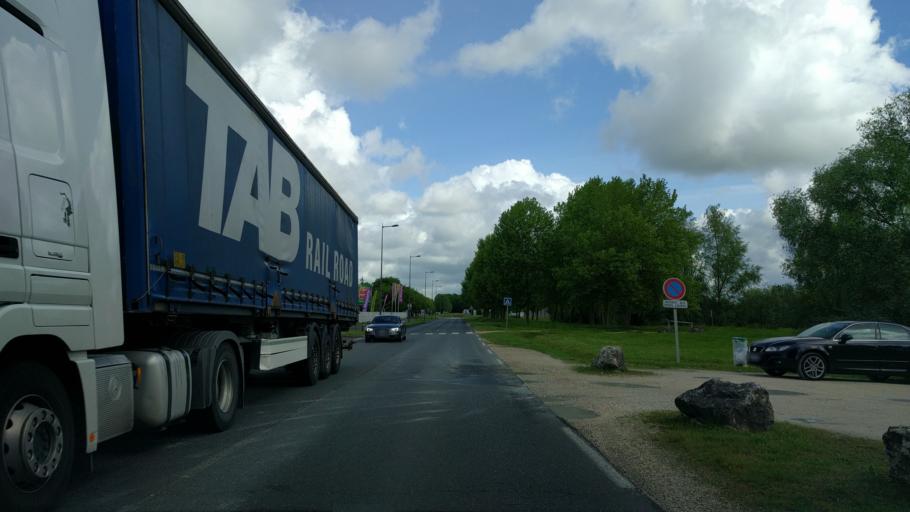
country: FR
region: Ile-de-France
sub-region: Departement de Seine-et-Marne
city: Savigny-le-Temple
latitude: 48.5822
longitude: 2.5937
